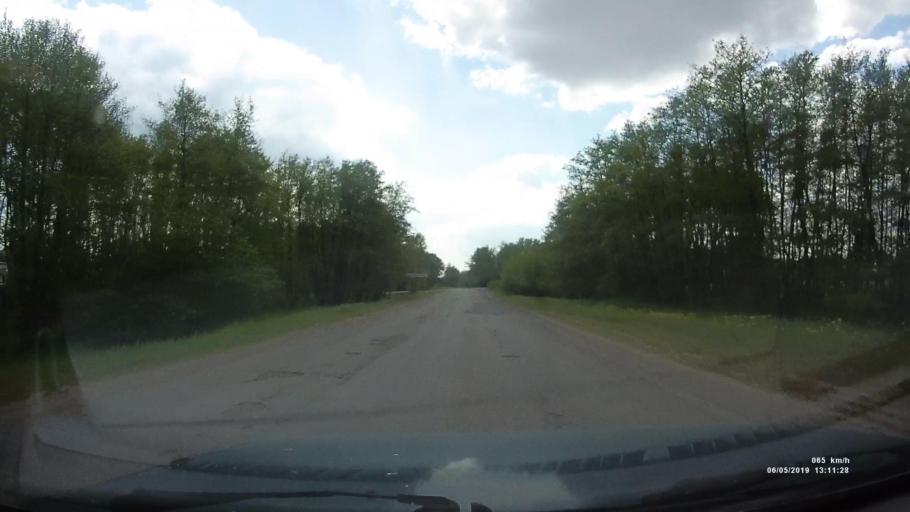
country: RU
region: Rostov
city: Ust'-Donetskiy
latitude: 47.7551
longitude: 40.9579
